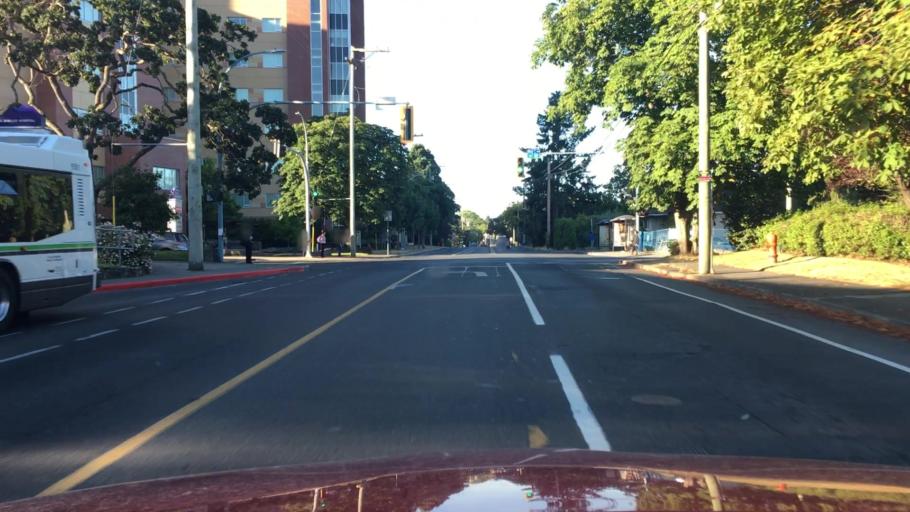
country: CA
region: British Columbia
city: Oak Bay
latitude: 48.4341
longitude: -123.3291
